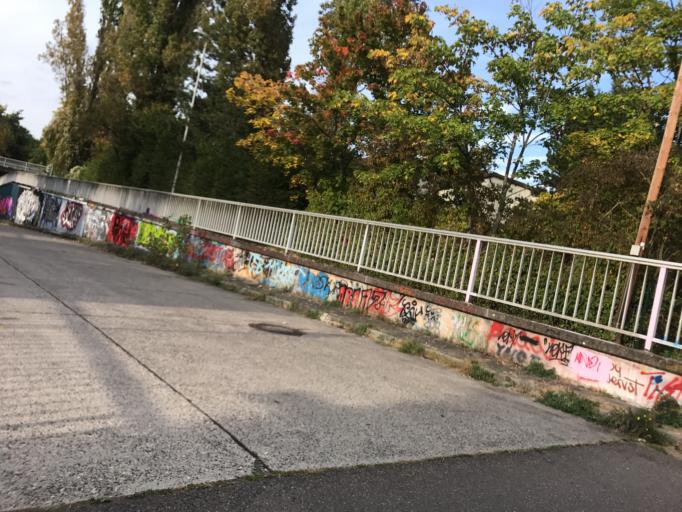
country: DE
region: Rheinland-Pfalz
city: Budenheim
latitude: 50.0101
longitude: 8.2134
